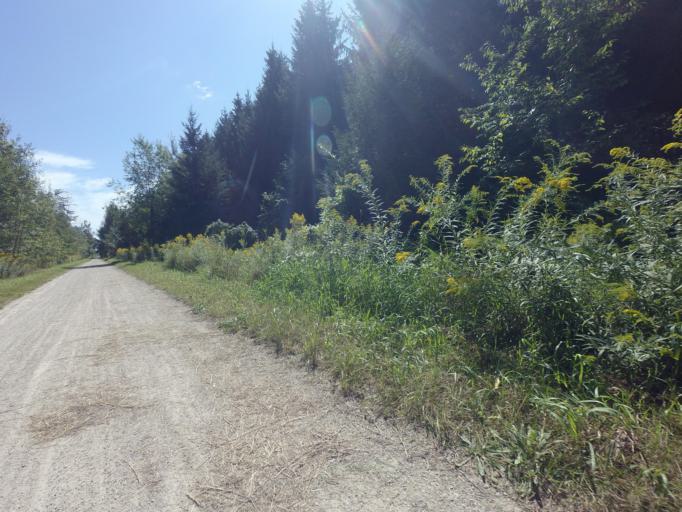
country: CA
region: Ontario
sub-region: Wellington County
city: Guelph
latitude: 43.7368
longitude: -80.3460
